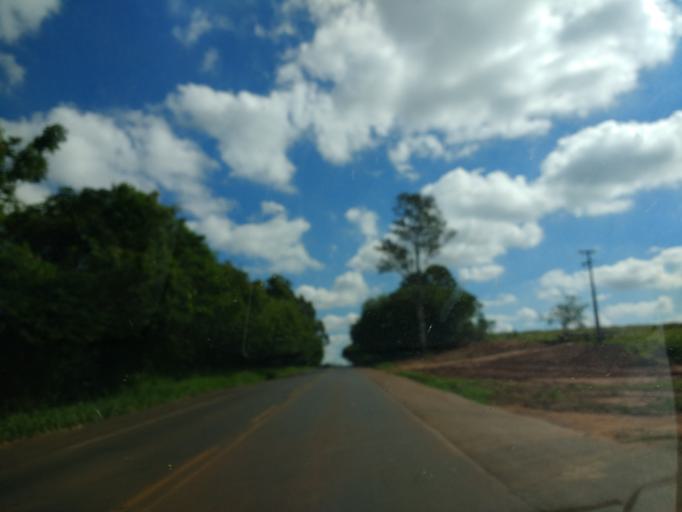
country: BR
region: Parana
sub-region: Alto Piquiri
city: Alto Piquiri
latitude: -23.8912
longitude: -53.4173
